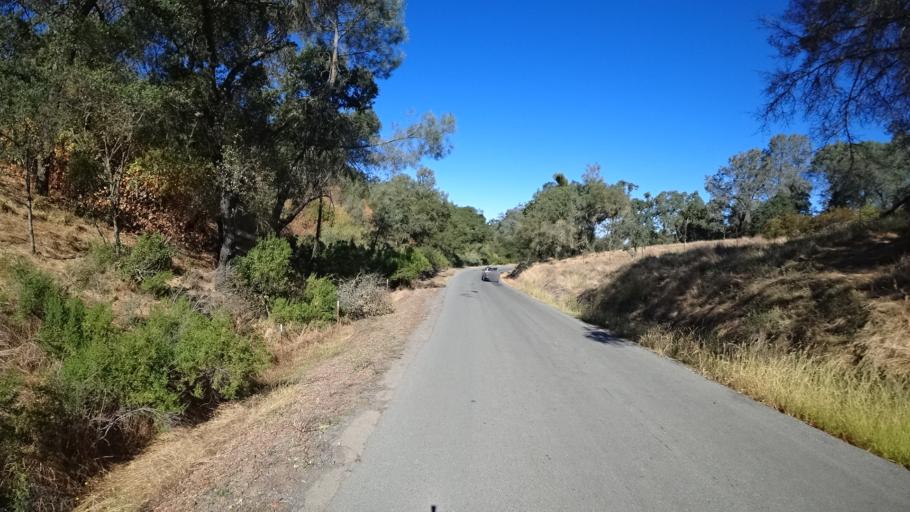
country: US
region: California
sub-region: Calaveras County
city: Rancho Calaveras
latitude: 38.1414
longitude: -120.8104
